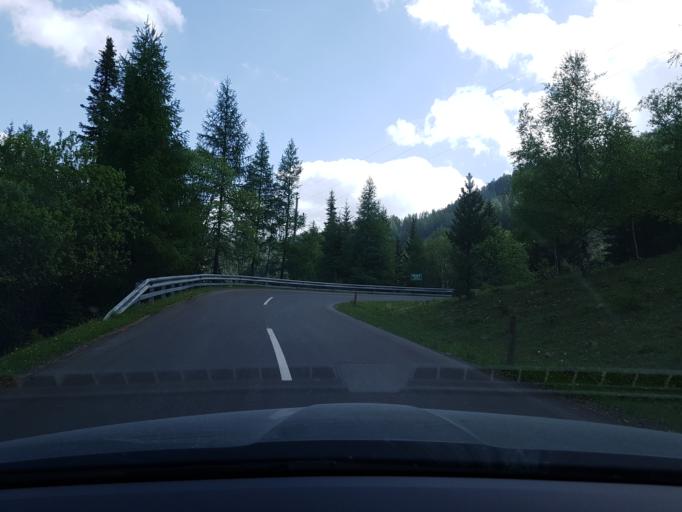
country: AT
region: Salzburg
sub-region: Politischer Bezirk Tamsweg
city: Thomatal
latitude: 46.9548
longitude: 13.7286
